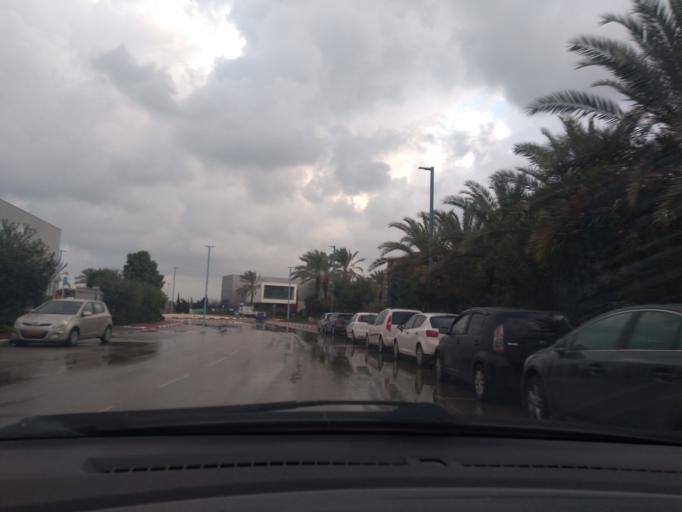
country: IL
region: Central District
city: Elyakhin
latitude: 32.4004
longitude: 34.8972
